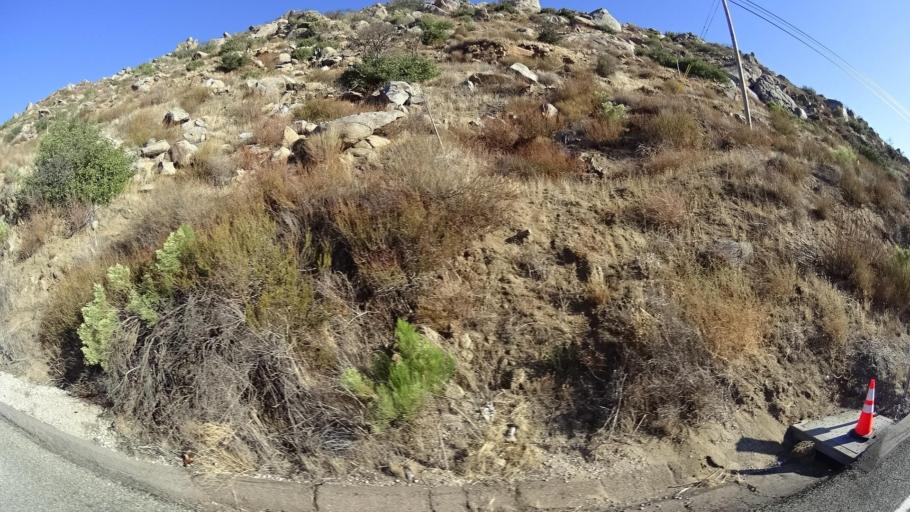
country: MX
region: Baja California
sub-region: Tecate
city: Hacienda Tecate
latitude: 32.5979
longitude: -116.5611
